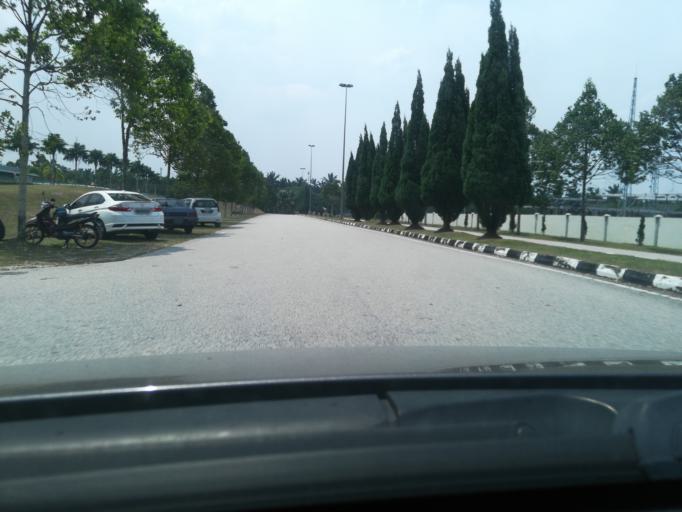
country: MY
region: Kedah
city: Kulim
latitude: 5.4296
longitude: 100.5777
